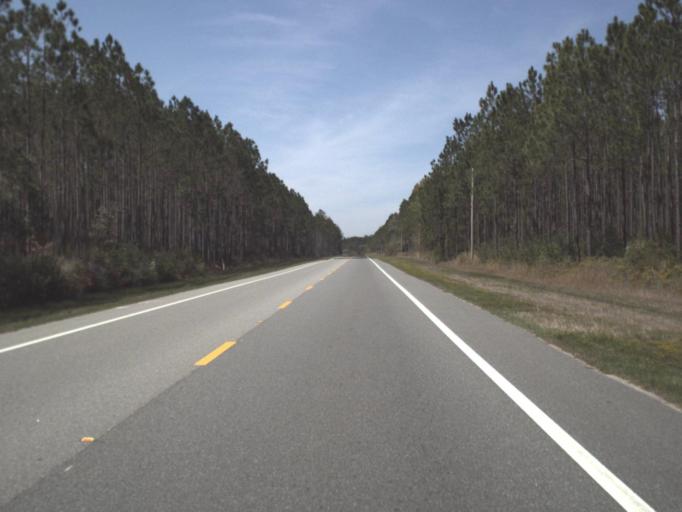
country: US
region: Florida
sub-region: Bay County
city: Lynn Haven
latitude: 30.3271
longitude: -85.7092
